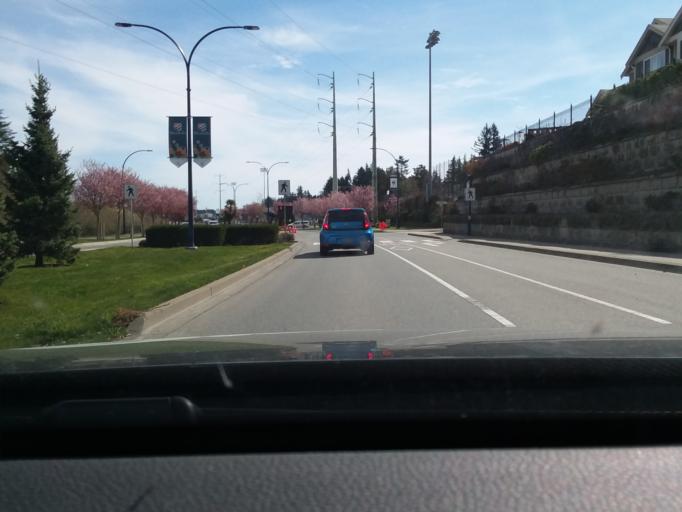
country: CA
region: British Columbia
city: Langford
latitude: 48.4441
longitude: -123.5287
